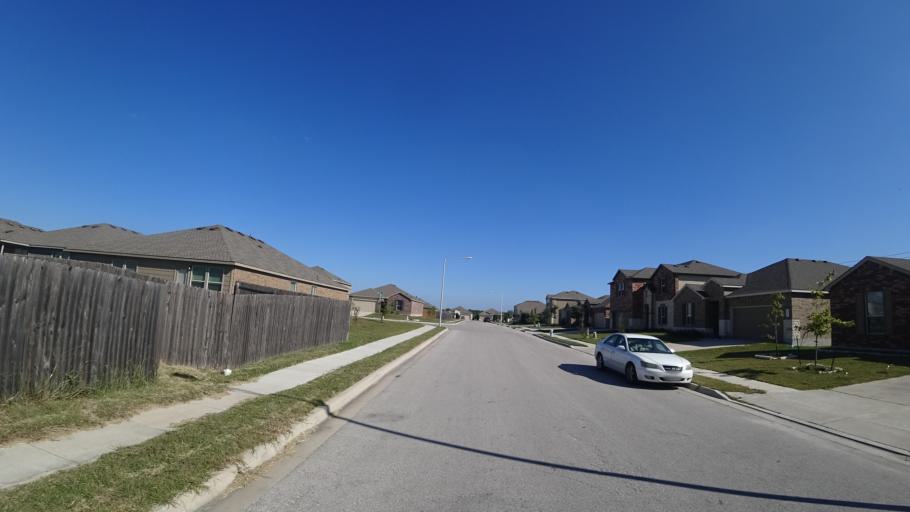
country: US
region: Texas
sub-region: Travis County
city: Manor
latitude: 30.3544
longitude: -97.6196
